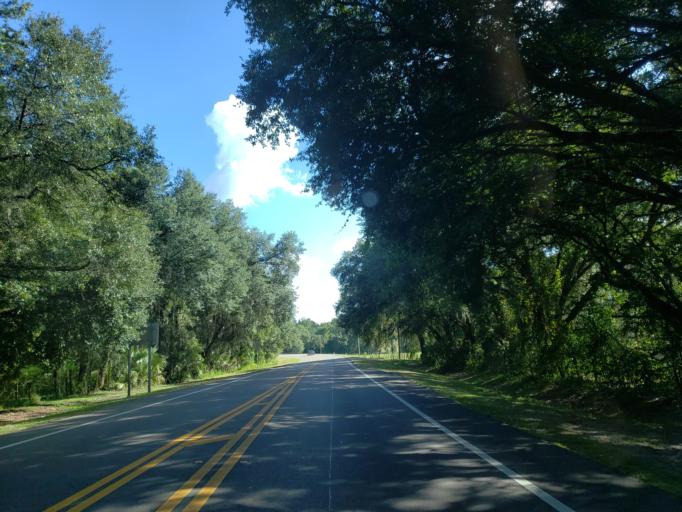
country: US
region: Florida
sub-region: Hillsborough County
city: Dover
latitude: 28.0185
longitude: -82.1752
